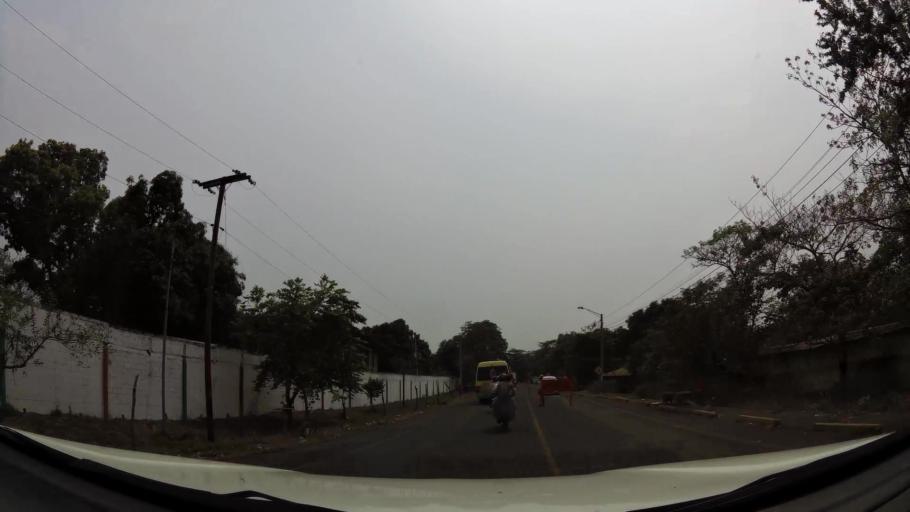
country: NI
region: Chinandega
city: Chinandega
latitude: 12.6405
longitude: -87.1295
